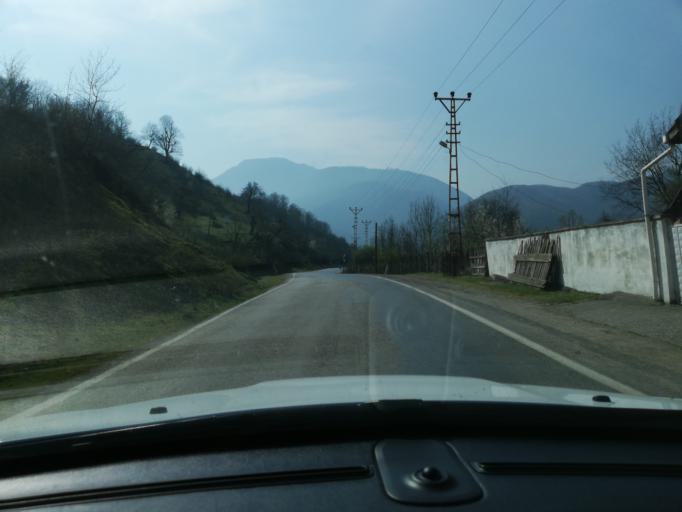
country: TR
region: Karabuk
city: Yenice
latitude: 41.2208
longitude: 32.3626
